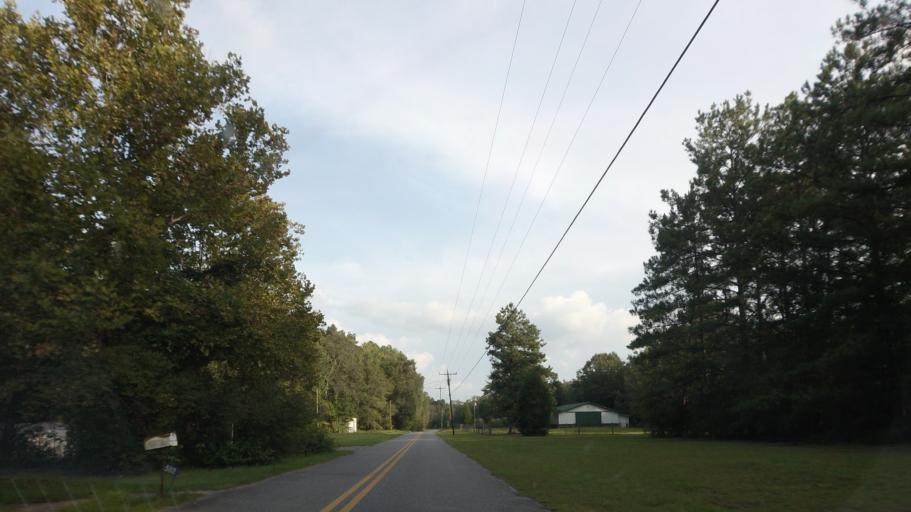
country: US
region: Georgia
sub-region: Wilkinson County
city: Gordon
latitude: 32.8330
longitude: -83.3933
